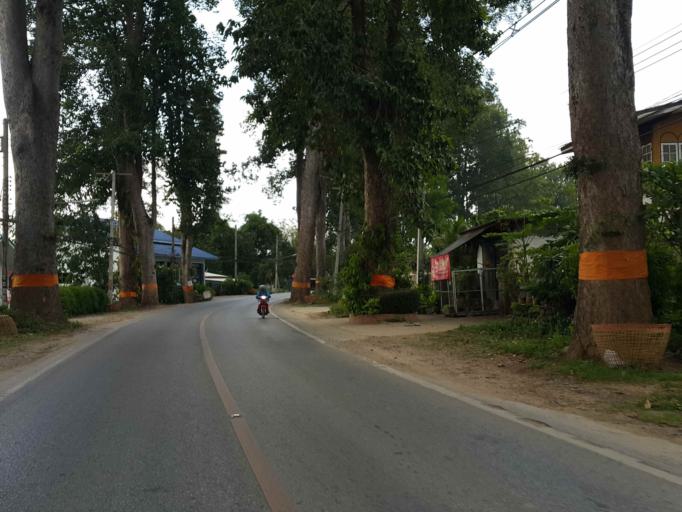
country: TH
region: Chiang Mai
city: Saraphi
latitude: 18.6889
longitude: 99.0422
